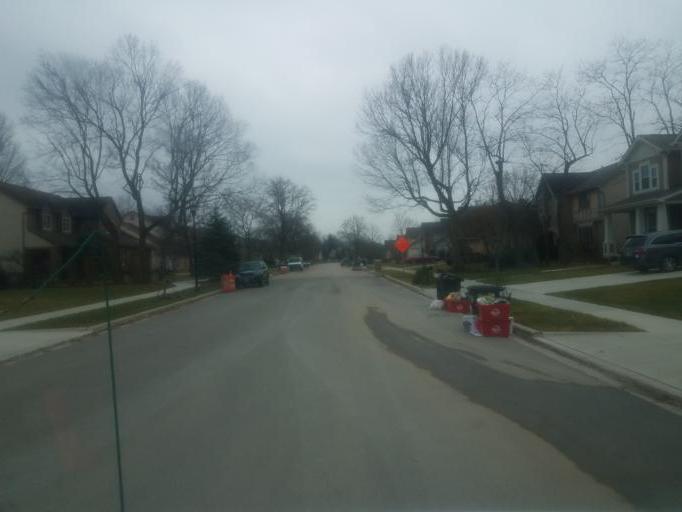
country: US
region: Ohio
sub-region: Franklin County
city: Westerville
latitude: 40.1310
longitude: -82.9589
